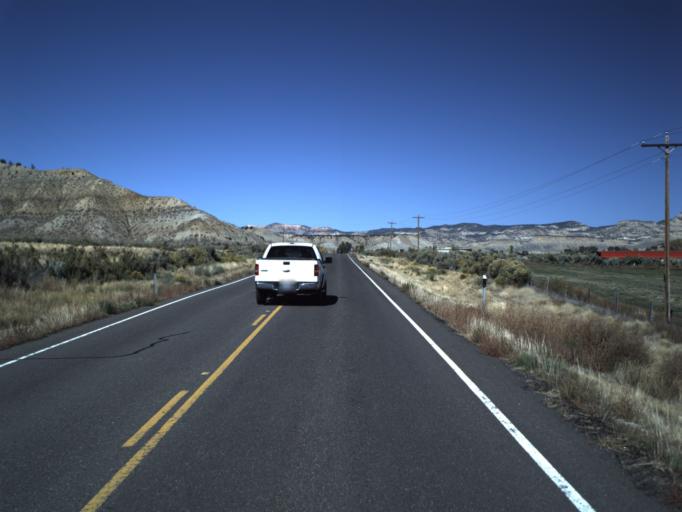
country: US
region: Utah
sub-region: Garfield County
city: Panguitch
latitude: 37.5985
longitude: -112.0614
